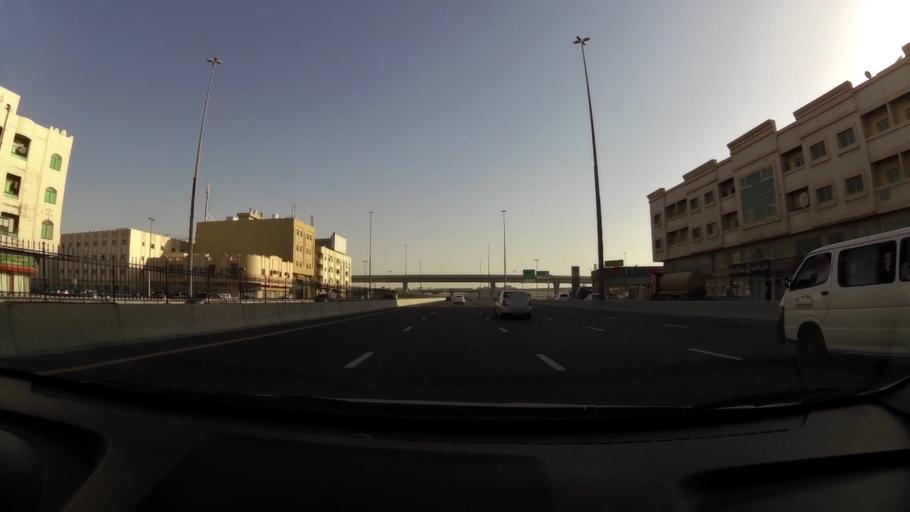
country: AE
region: Ash Shariqah
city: Sharjah
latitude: 25.3121
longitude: 55.4484
